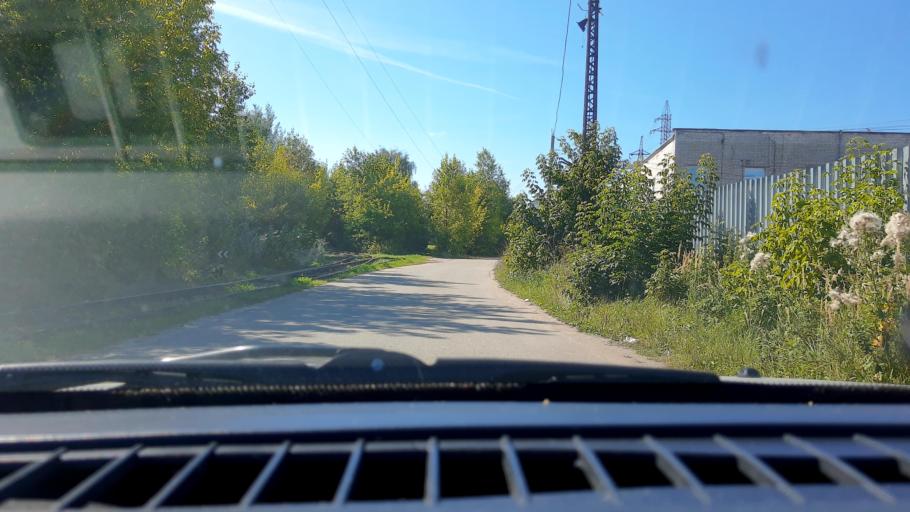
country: RU
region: Nizjnij Novgorod
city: Neklyudovo
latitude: 56.3514
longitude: 43.8823
